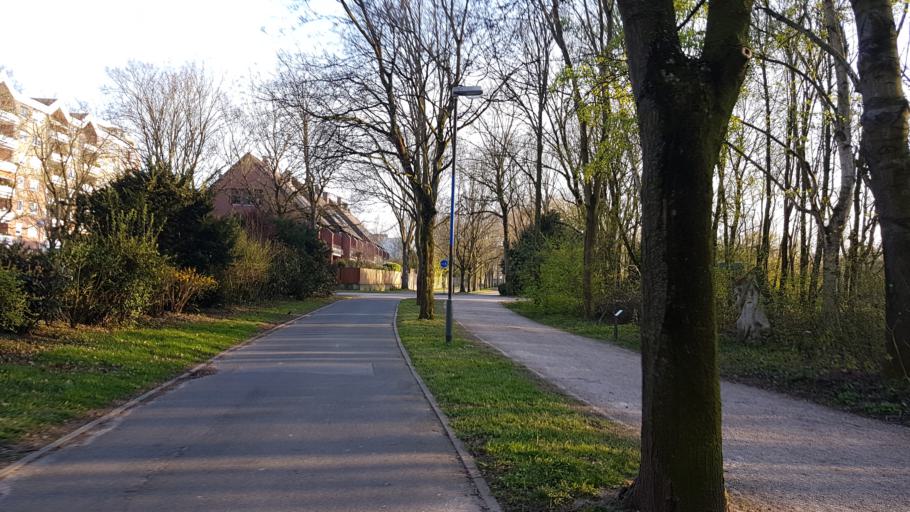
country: DE
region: Lower Saxony
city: Langenhagen
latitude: 52.4433
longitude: 9.7493
